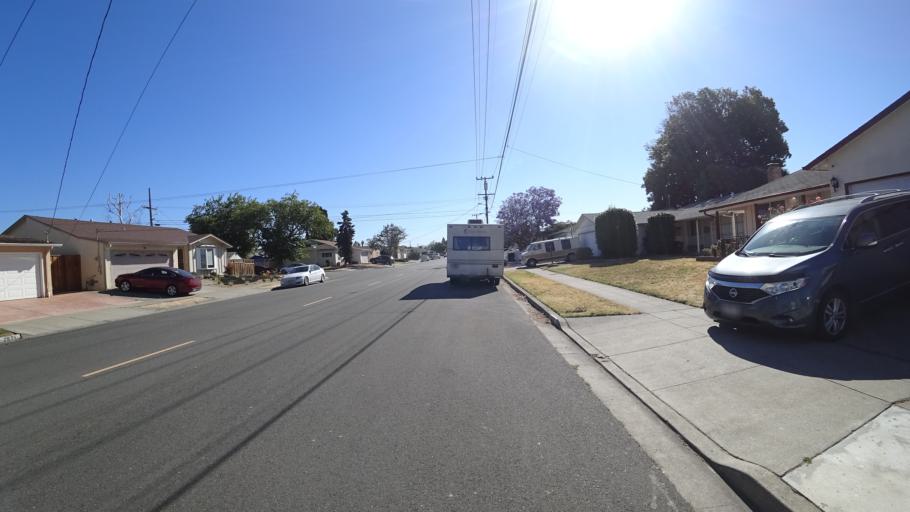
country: US
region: California
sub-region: Alameda County
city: Hayward
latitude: 37.6336
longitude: -122.1086
